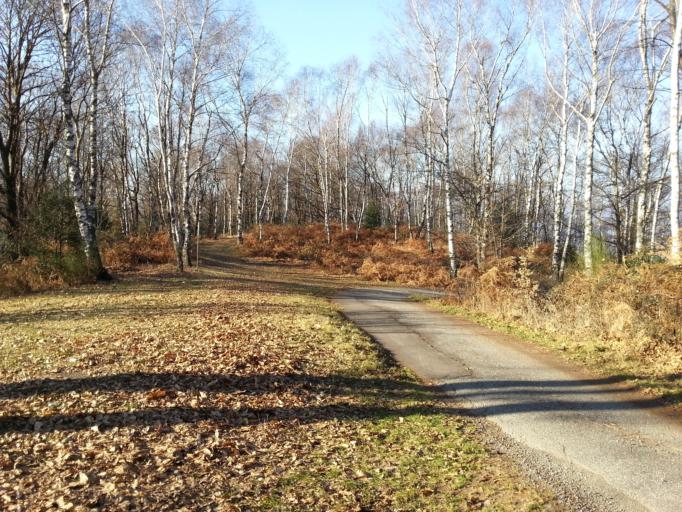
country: CH
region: Ticino
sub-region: Bellinzona District
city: Cadenazzo
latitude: 46.1394
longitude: 8.9260
